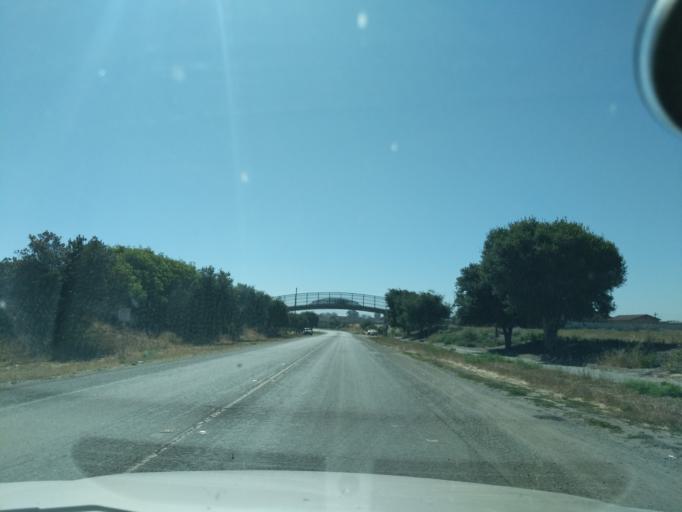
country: US
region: California
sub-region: Monterey County
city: Boronda
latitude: 36.6992
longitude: -121.6747
